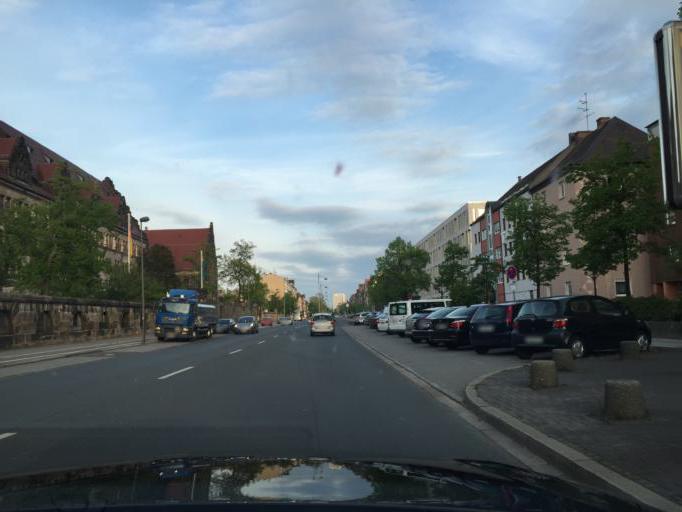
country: DE
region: Bavaria
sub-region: Regierungsbezirk Mittelfranken
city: Wetzendorf
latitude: 49.4546
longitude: 11.0444
